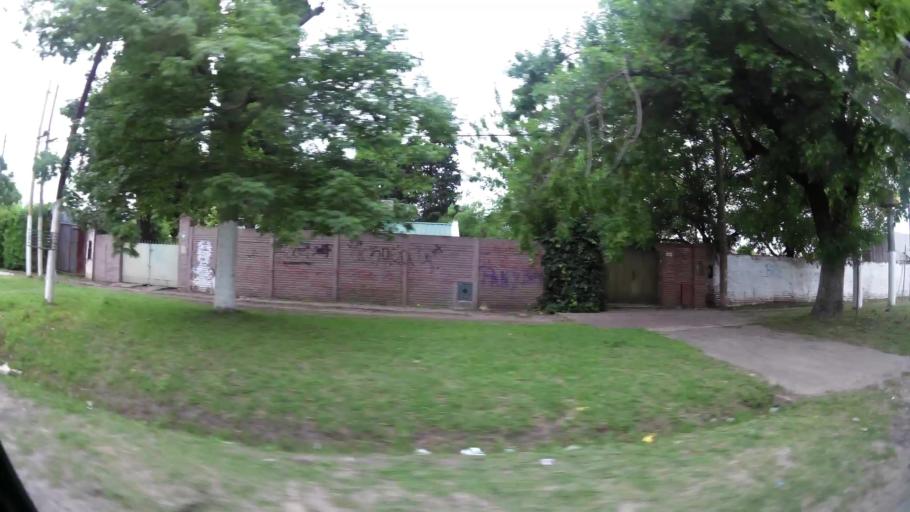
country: AR
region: Buenos Aires
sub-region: Partido de La Plata
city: La Plata
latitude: -34.9322
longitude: -58.0037
